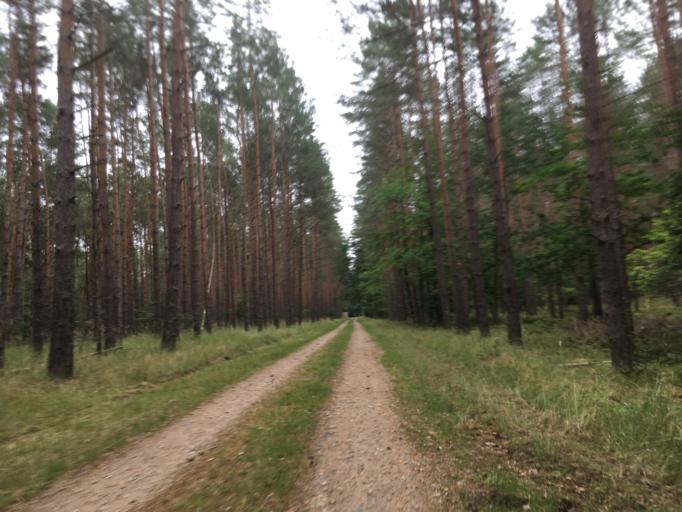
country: DE
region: Brandenburg
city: Zehdenick
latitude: 53.0363
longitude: 13.3699
